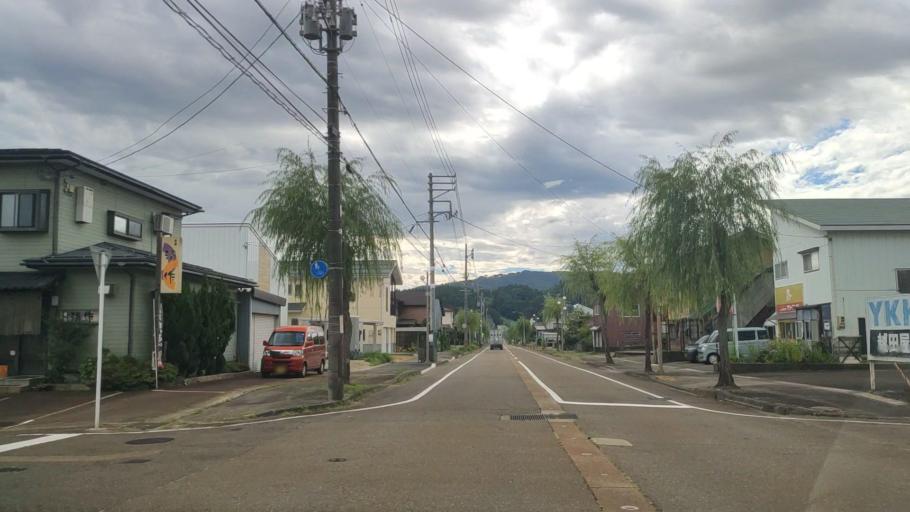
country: JP
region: Niigata
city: Arai
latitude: 37.0181
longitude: 138.2481
